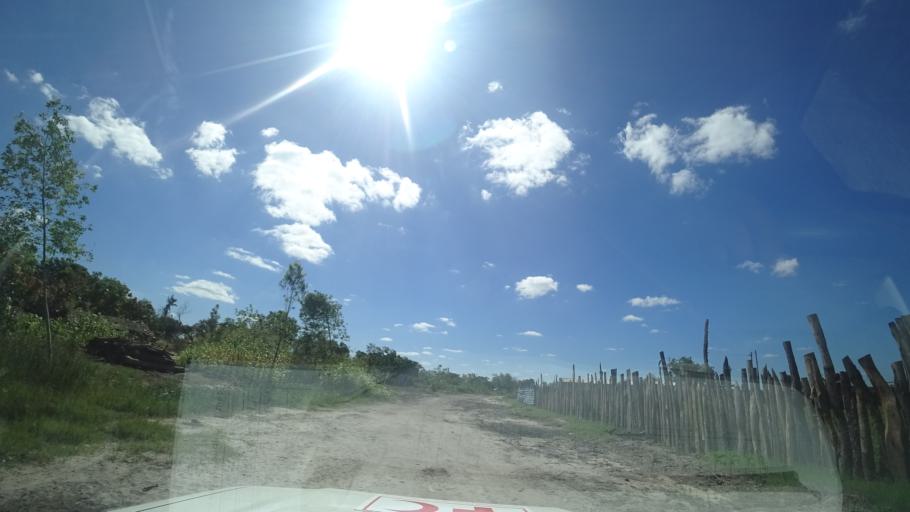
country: MZ
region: Sofala
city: Dondo
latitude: -19.5025
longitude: 34.6124
